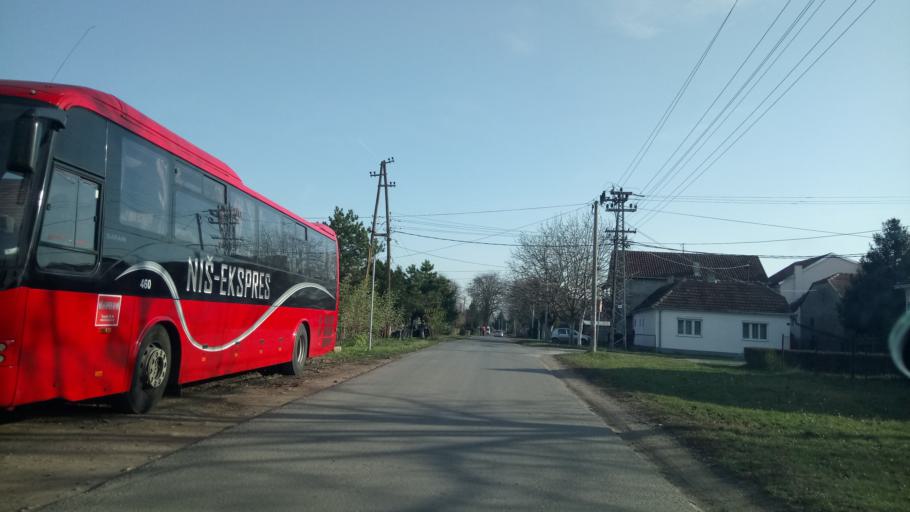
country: RS
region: Autonomna Pokrajina Vojvodina
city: Nova Pazova
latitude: 44.9529
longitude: 20.2260
